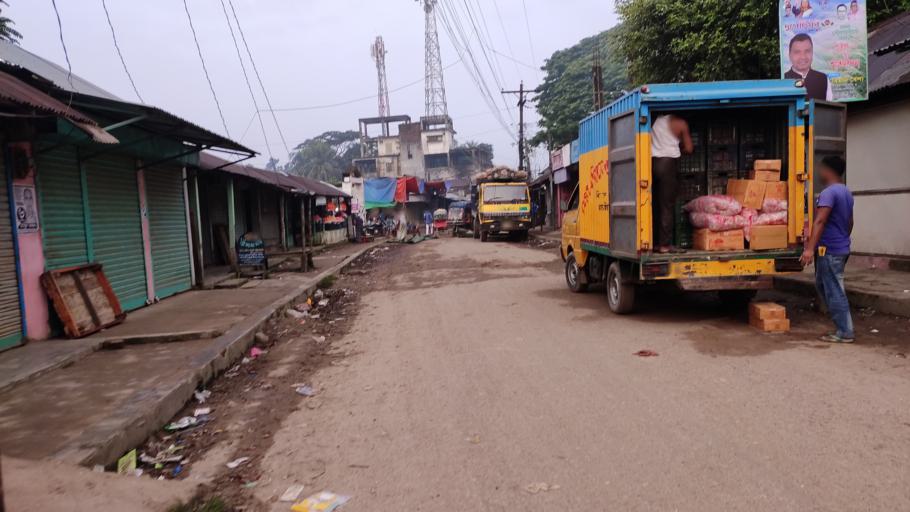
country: BD
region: Dhaka
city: Netrakona
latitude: 24.7165
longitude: 90.9551
